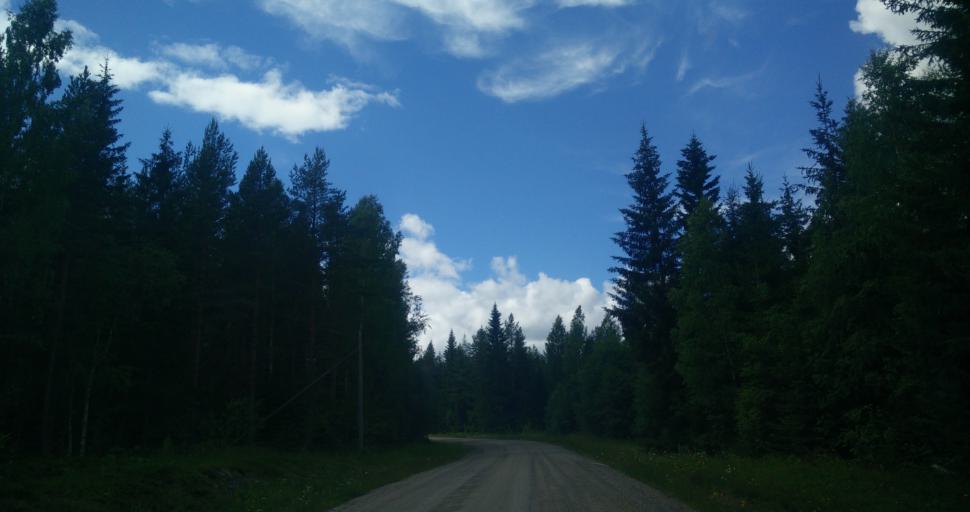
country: SE
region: Vaesternorrland
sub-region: Sundsvalls Kommun
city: Vi
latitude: 62.1472
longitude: 17.1400
